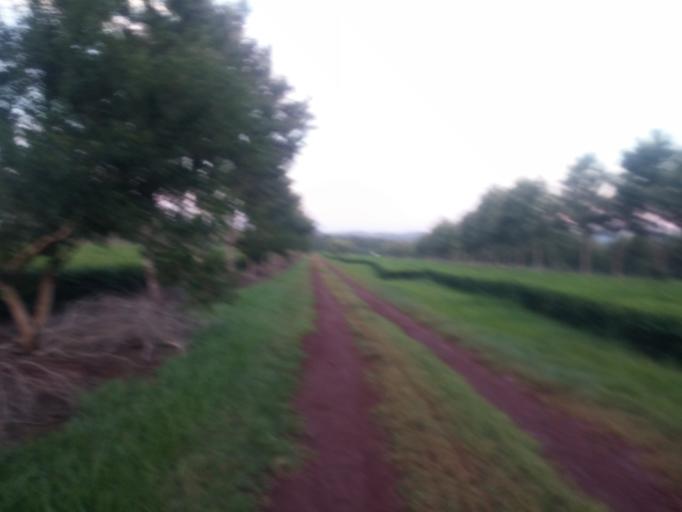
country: AR
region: Misiones
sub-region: Departamento de Obera
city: Obera
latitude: -27.4440
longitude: -55.0880
